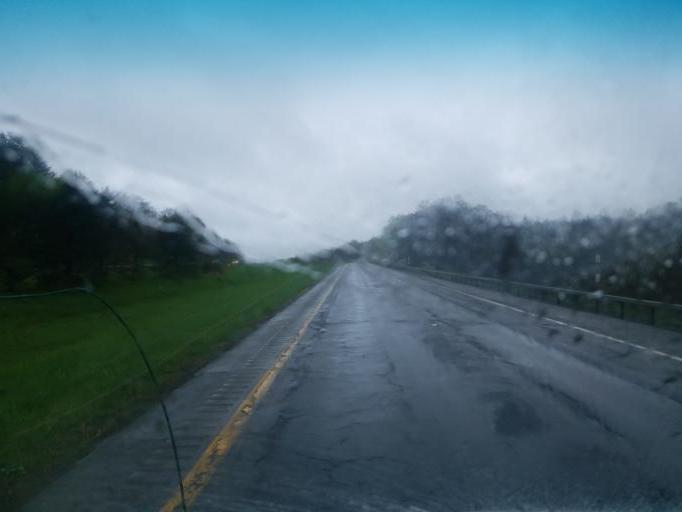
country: US
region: New York
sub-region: Chautauqua County
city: Lakewood
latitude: 42.1329
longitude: -79.3293
